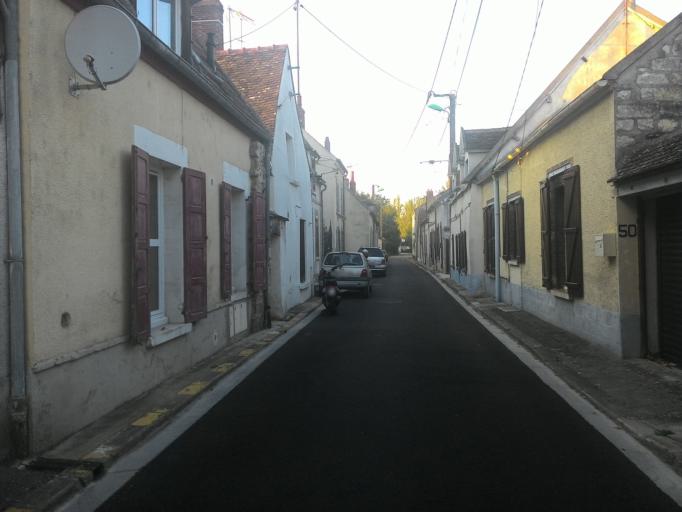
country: FR
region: Bourgogne
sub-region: Departement de l'Yonne
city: Sens
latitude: 48.1995
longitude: 3.2748
